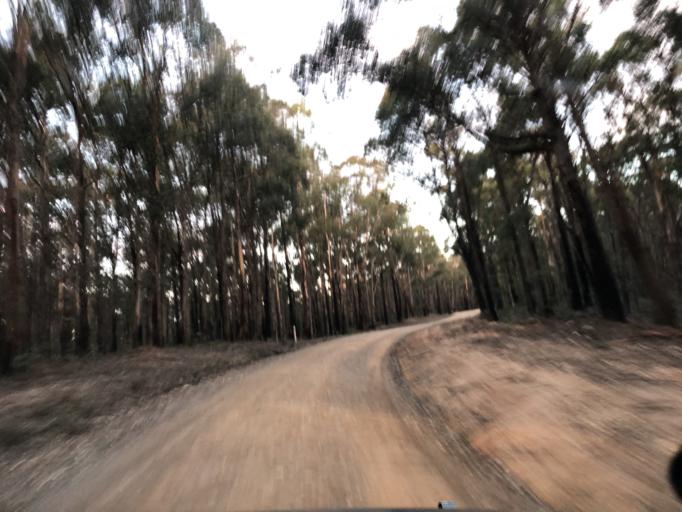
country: AU
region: Victoria
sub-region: Moorabool
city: Bacchus Marsh
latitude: -37.4722
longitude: 144.4217
